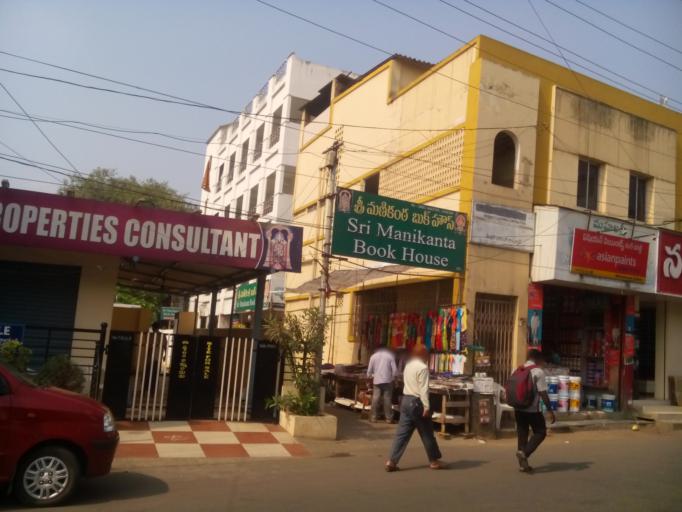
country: IN
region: Andhra Pradesh
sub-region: East Godavari
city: Rajahmundry
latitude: 16.9968
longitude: 81.7736
